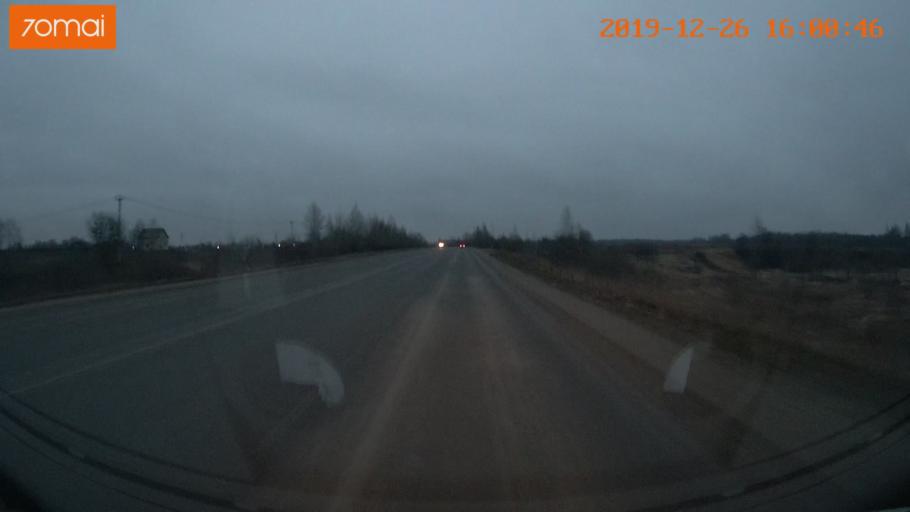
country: RU
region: Jaroslavl
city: Rybinsk
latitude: 58.0207
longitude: 38.8077
